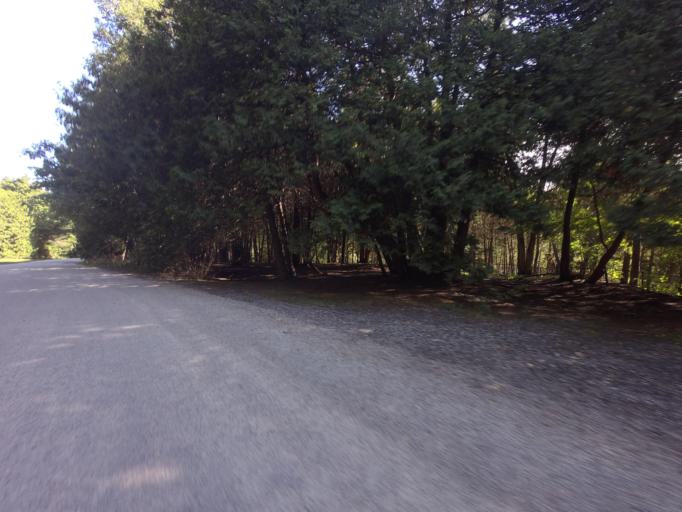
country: CA
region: Ontario
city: Waterloo
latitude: 43.6663
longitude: -80.4534
